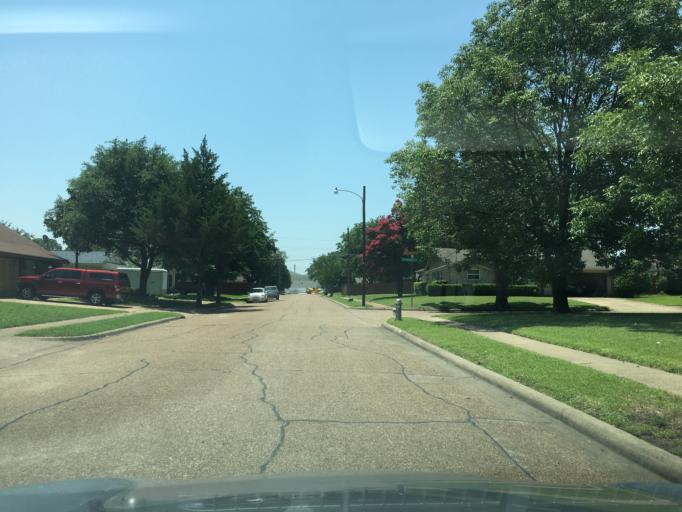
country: US
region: Texas
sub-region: Dallas County
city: Garland
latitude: 32.9119
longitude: -96.6899
